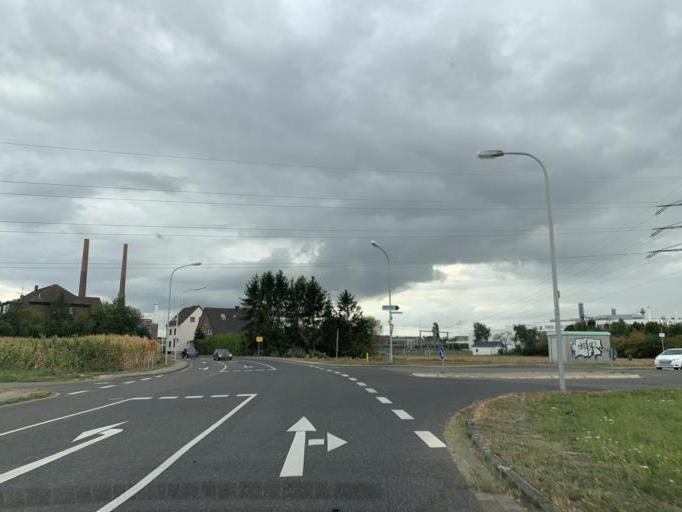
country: DE
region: North Rhine-Westphalia
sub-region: Regierungsbezirk Koln
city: Heinsberg
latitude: 51.0649
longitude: 6.1369
